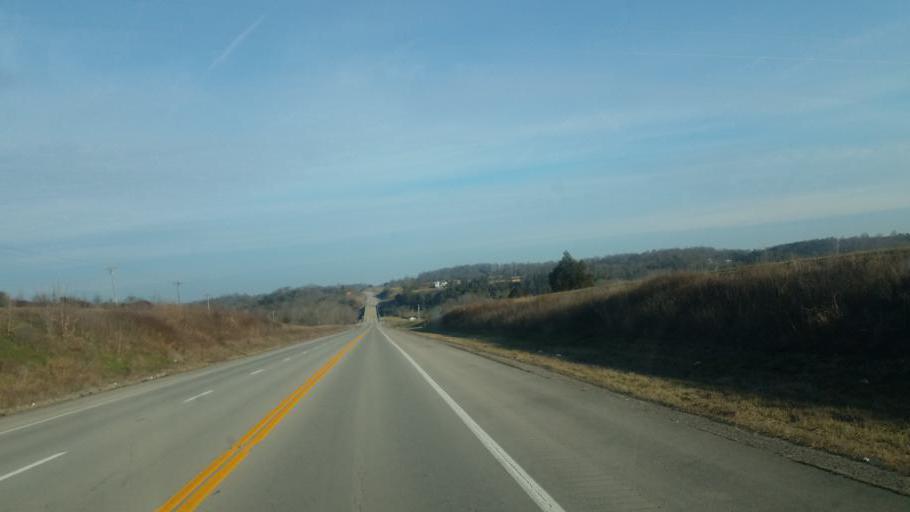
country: US
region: Kentucky
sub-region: Russell County
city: Jamestown
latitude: 36.9615
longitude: -85.0890
